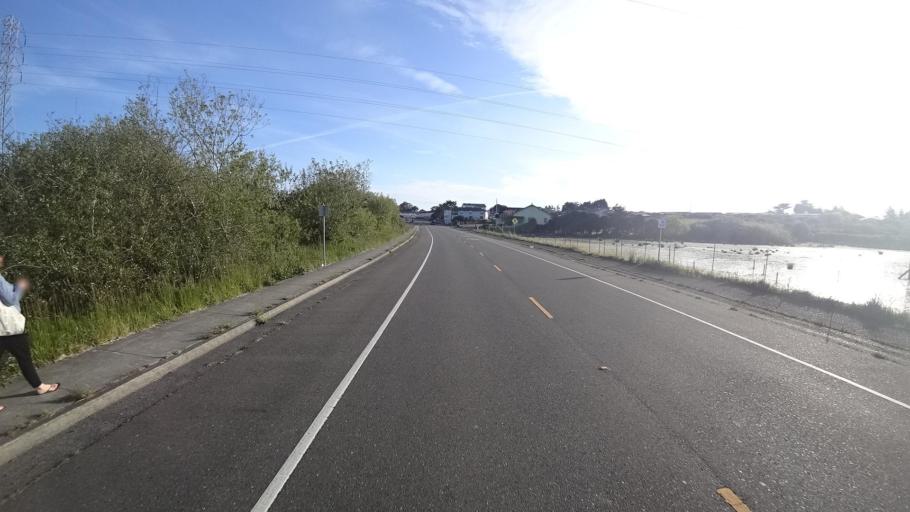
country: US
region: California
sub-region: Humboldt County
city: Humboldt Hill
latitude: 40.7379
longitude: -124.2007
